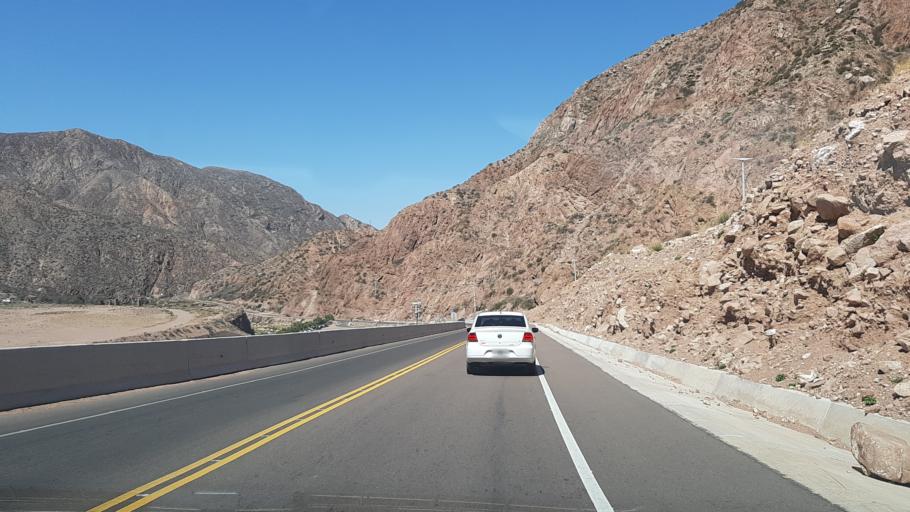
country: AR
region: Mendoza
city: Lujan de Cuyo
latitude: -33.0016
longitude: -69.1290
